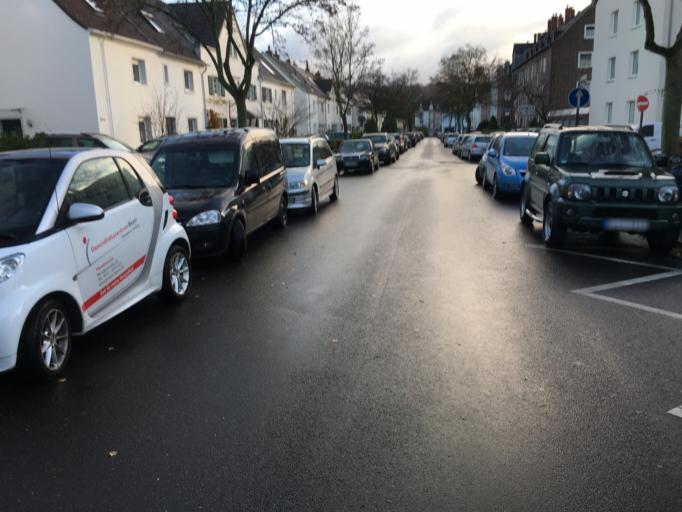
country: DE
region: North Rhine-Westphalia
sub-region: Regierungsbezirk Dusseldorf
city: Erkrath
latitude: 51.2382
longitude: 6.8562
